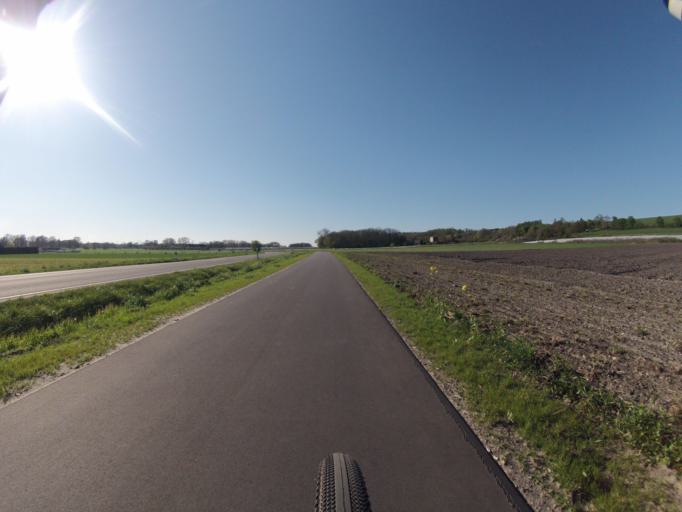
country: DE
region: North Rhine-Westphalia
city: Ibbenburen
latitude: 52.2240
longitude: 7.7300
